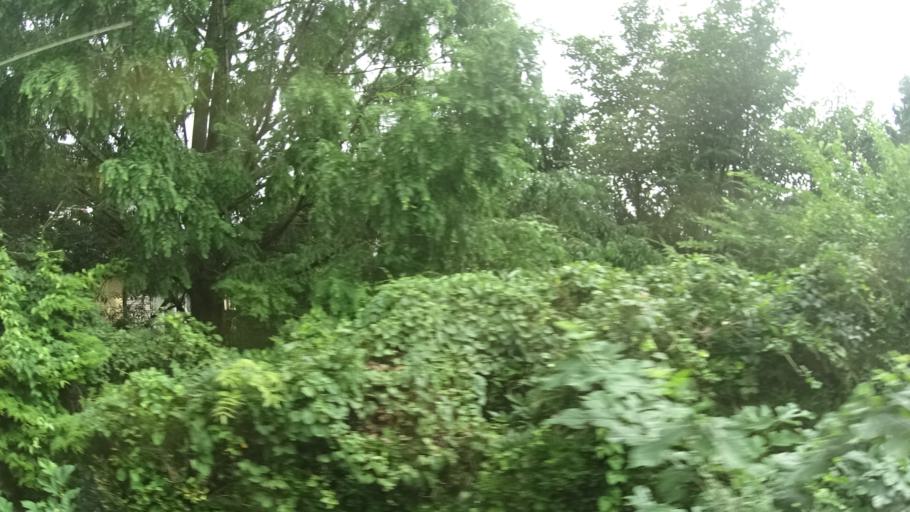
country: JP
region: Tochigi
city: Imaichi
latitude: 36.7226
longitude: 139.6835
